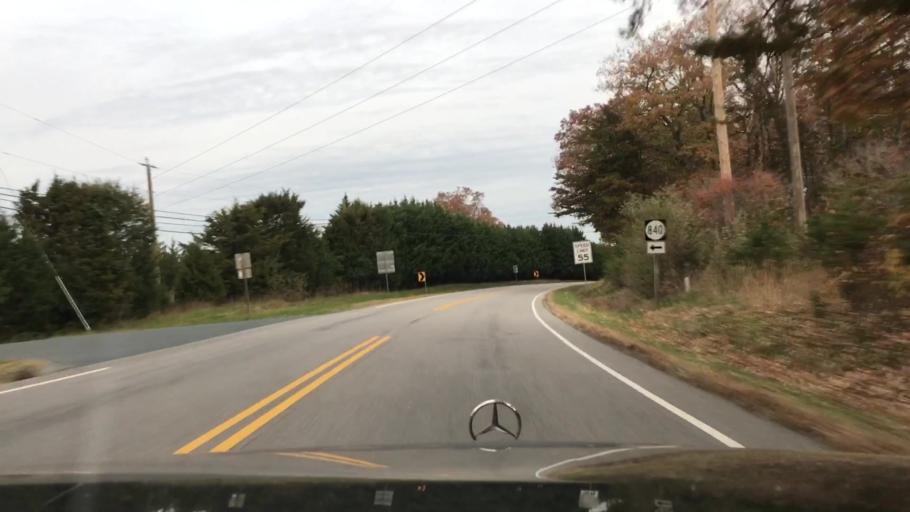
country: US
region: Virginia
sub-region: Campbell County
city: Altavista
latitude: 37.1412
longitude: -79.3080
